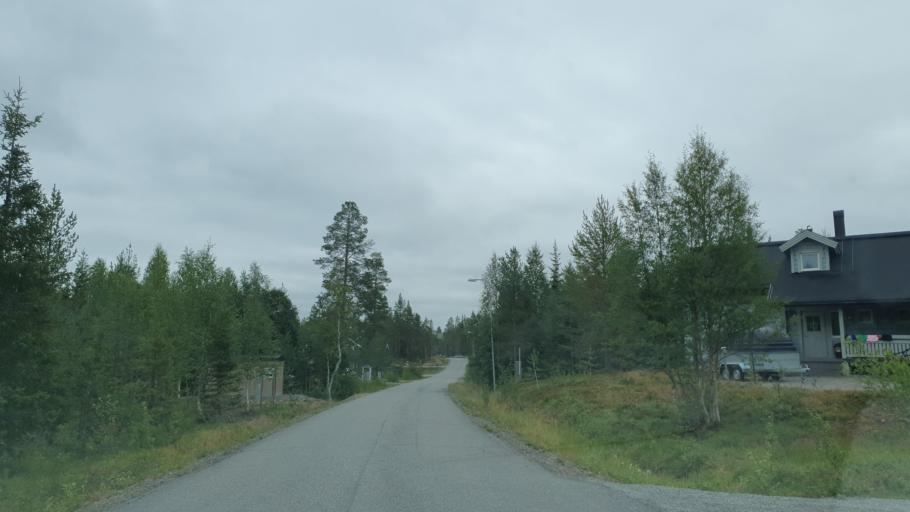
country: FI
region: Lapland
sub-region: Tunturi-Lappi
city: Kolari
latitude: 67.5939
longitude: 24.1706
